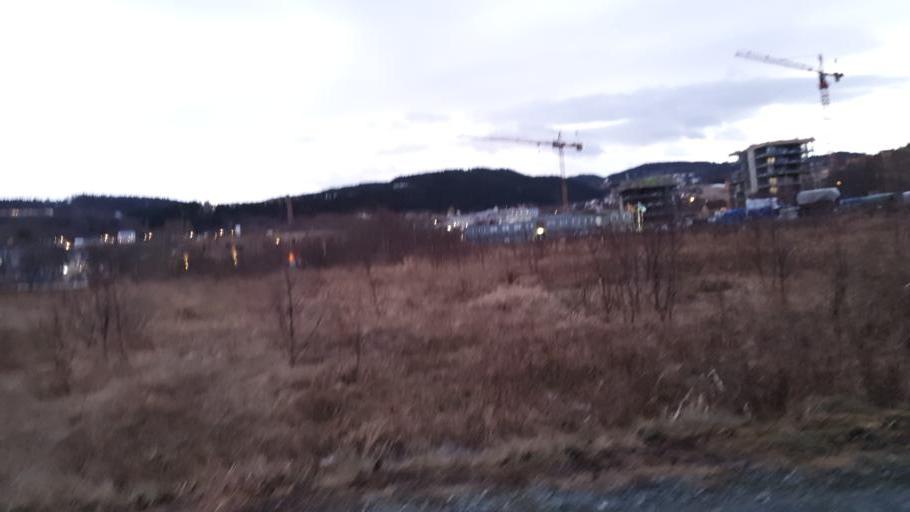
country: NO
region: Sor-Trondelag
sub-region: Trondheim
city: Trondheim
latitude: 63.4306
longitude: 10.5309
